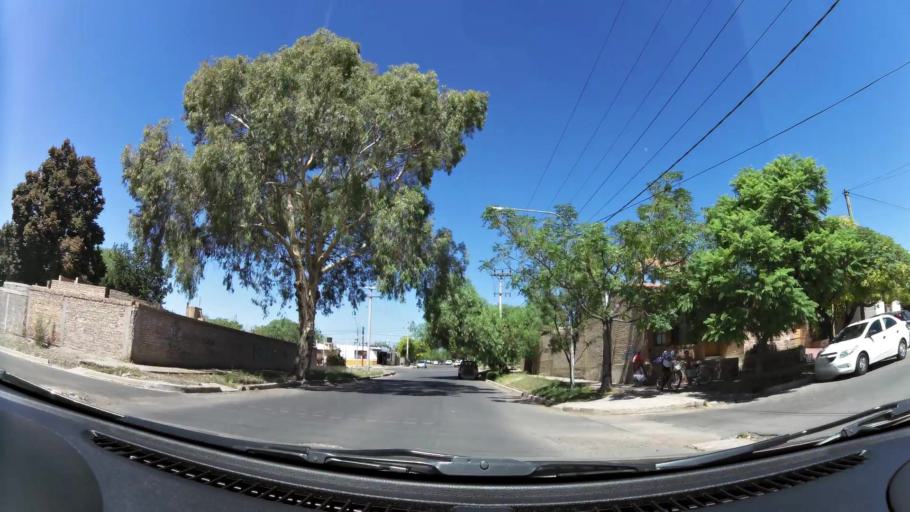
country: AR
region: Mendoza
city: Las Heras
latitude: -32.8411
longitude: -68.8718
